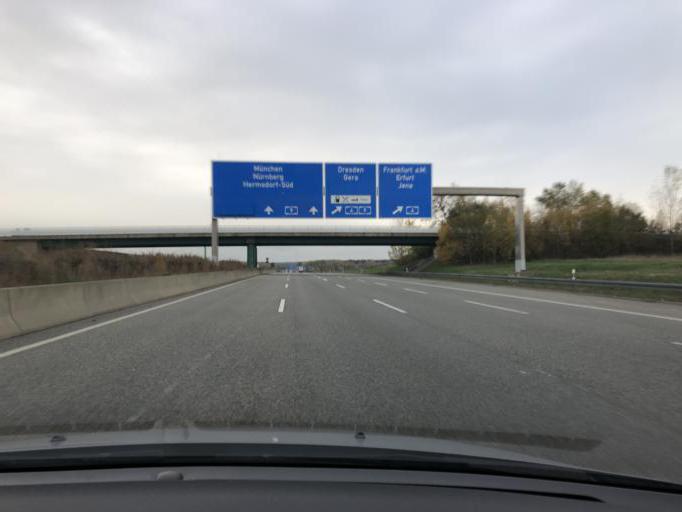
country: DE
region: Thuringia
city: Hermsdorf
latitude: 50.8905
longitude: 11.8449
